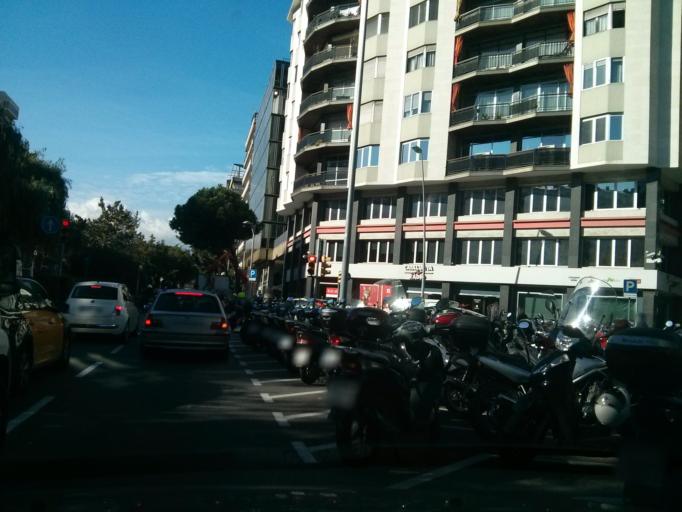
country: ES
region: Catalonia
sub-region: Provincia de Barcelona
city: Sarria-Sant Gervasi
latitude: 41.3924
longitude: 2.1419
